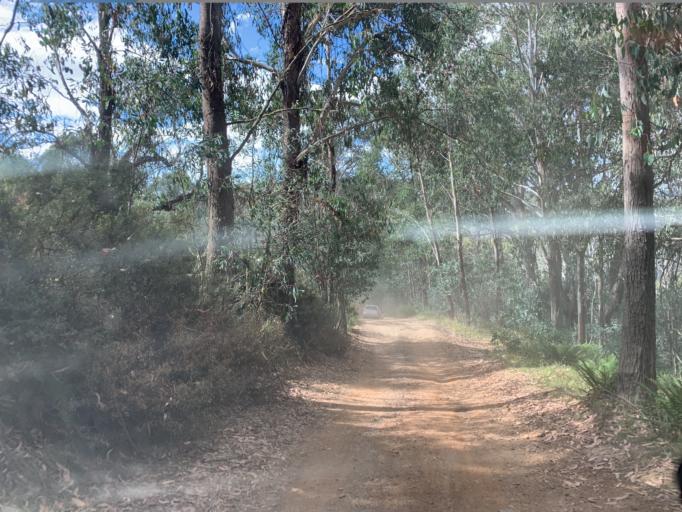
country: AU
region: Victoria
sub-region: Mansfield
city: Mansfield
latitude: -37.1083
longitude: 146.5348
